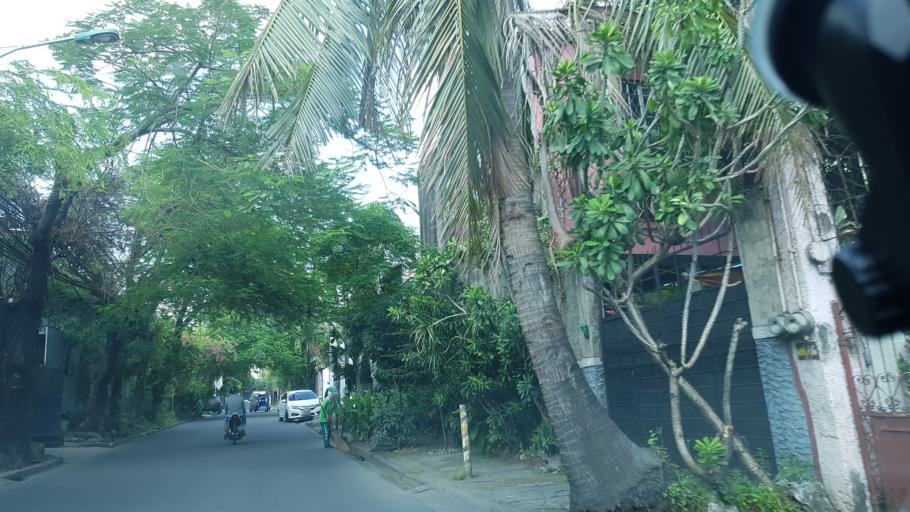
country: PH
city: Sambayanihan People's Village
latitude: 14.4766
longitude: 121.0277
